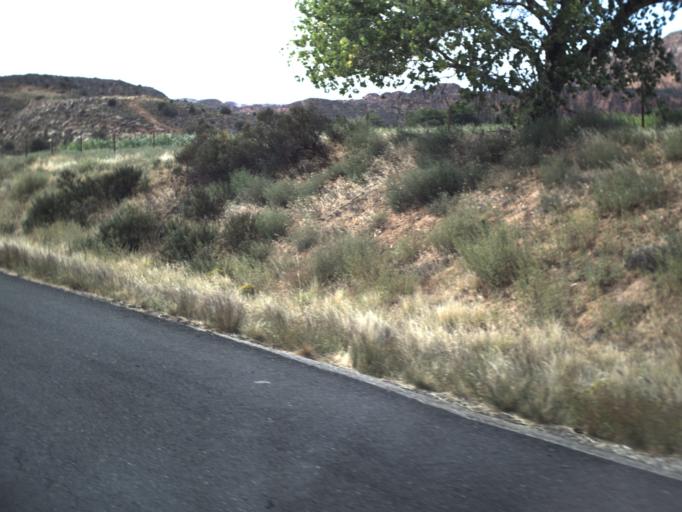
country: US
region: Utah
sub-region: Washington County
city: Toquerville
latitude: 37.2465
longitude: -113.3497
